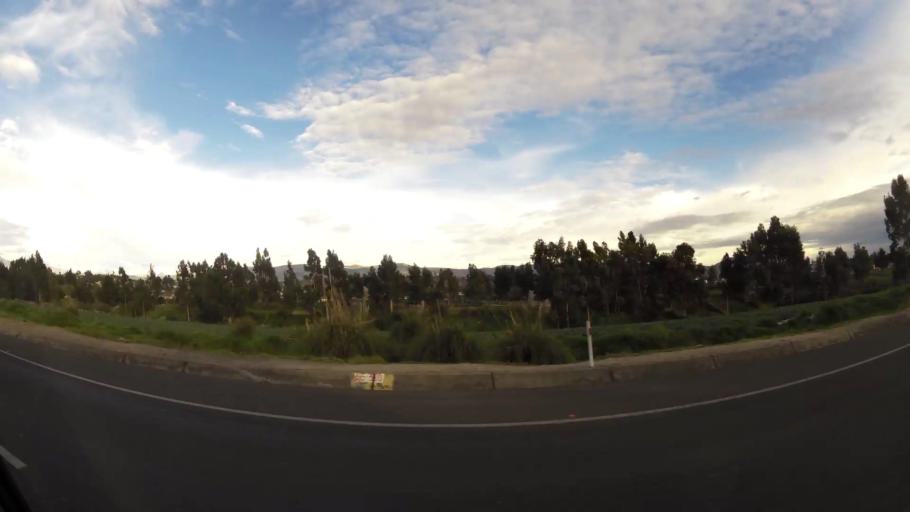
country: EC
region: Cotopaxi
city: Saquisili
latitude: -0.8599
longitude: -78.6232
